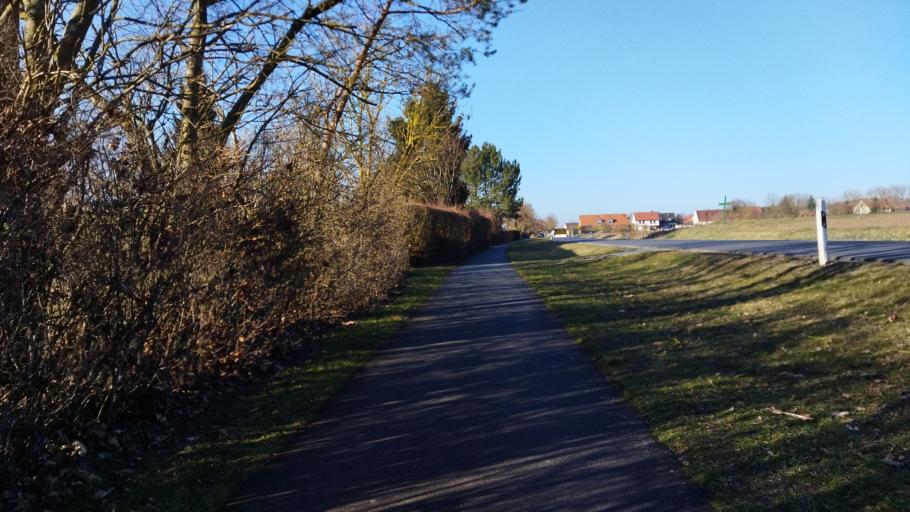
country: DE
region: Bavaria
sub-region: Regierungsbezirk Unterfranken
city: Albertshofen
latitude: 49.7596
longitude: 10.1600
